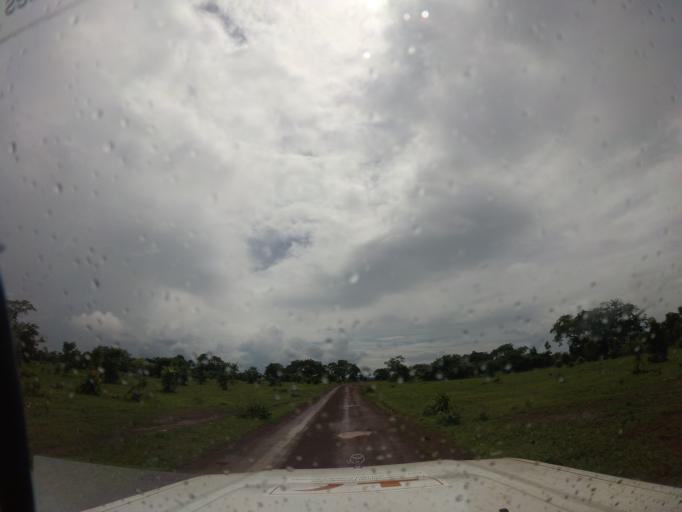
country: SL
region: Northern Province
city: Loma
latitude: 9.8753
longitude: -12.4368
